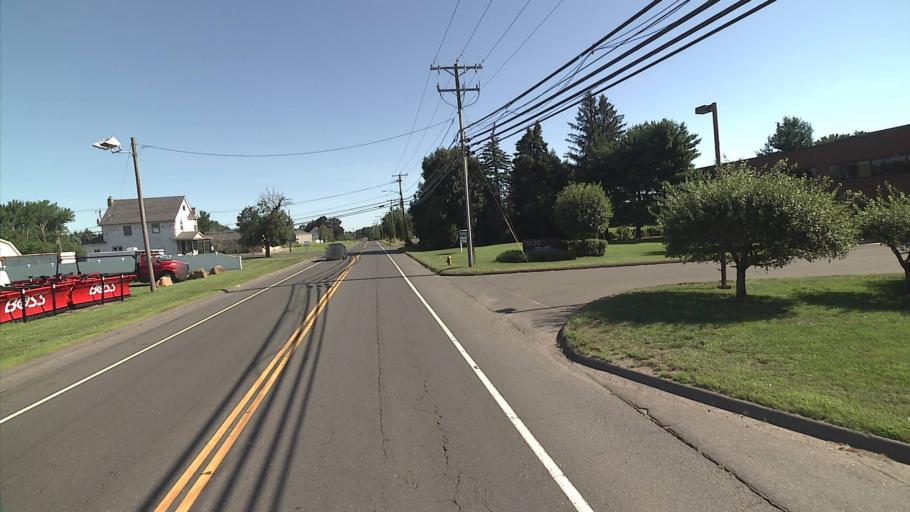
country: US
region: Connecticut
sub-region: New Haven County
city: Cheshire Village
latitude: 41.5428
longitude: -72.8924
